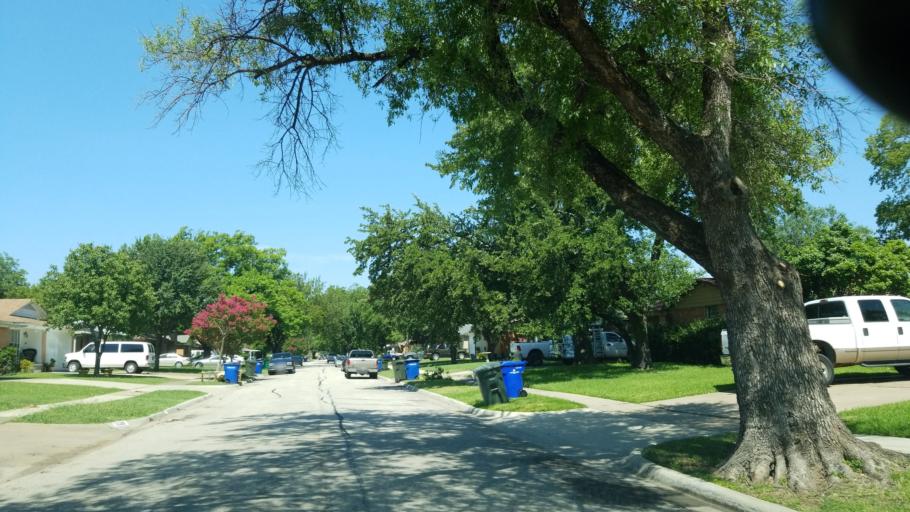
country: US
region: Texas
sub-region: Dallas County
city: Carrollton
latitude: 32.9676
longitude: -96.9024
